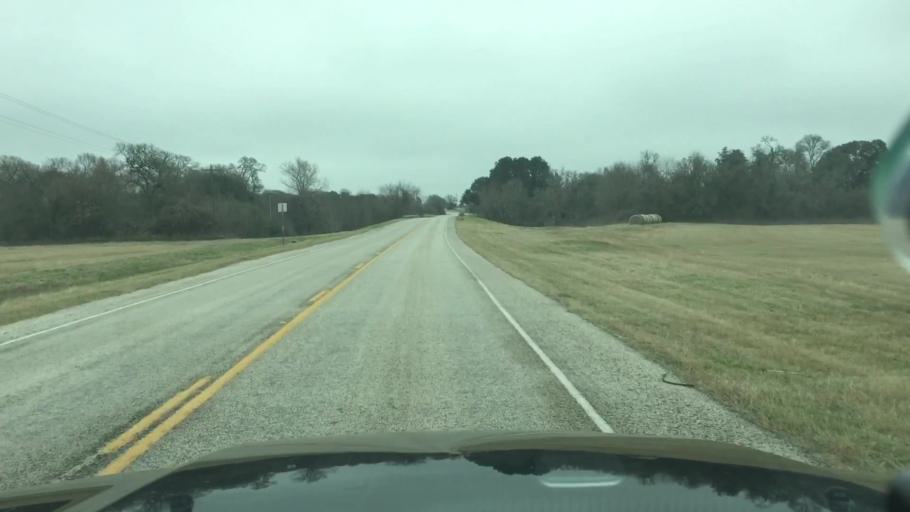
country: US
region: Texas
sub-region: Fayette County
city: La Grange
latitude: 30.0100
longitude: -96.9116
